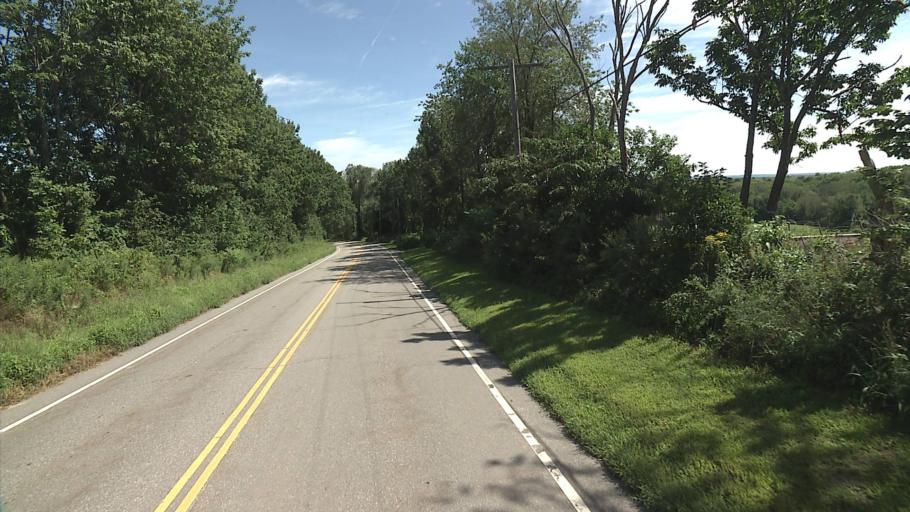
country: US
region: Connecticut
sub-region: Windham County
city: South Woodstock
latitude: 41.8276
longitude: -72.0261
